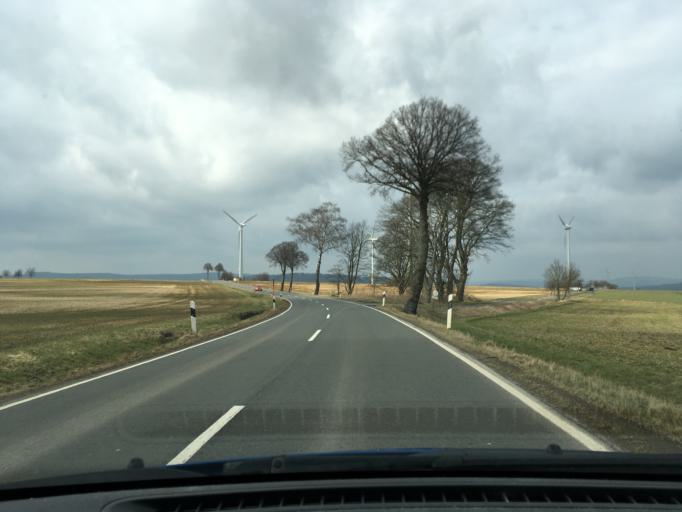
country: DE
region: Lower Saxony
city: Dransfeld
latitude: 51.5099
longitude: 9.7499
